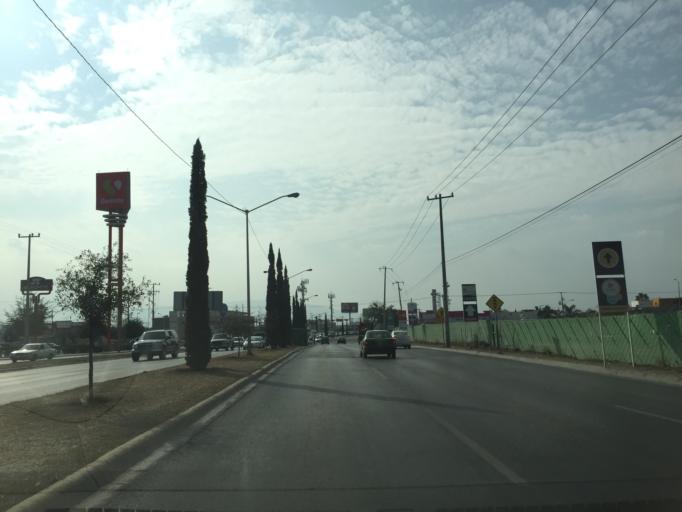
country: MX
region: Nuevo Leon
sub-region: Apodaca
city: Fraccionamiento Cosmopolis Octavo Sector
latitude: 25.7842
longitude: -100.2363
